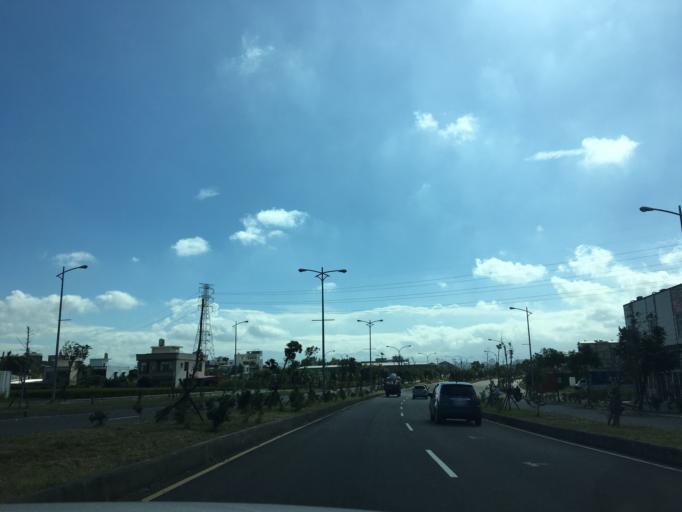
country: TW
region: Taiwan
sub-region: Hsinchu
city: Zhubei
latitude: 24.7939
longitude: 121.0211
